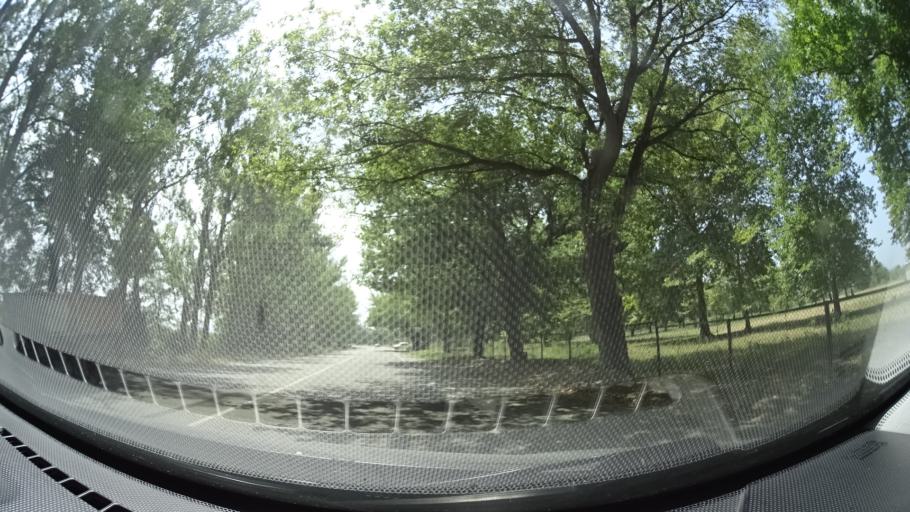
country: GE
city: Bagdadi
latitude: 41.7153
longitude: 46.0892
